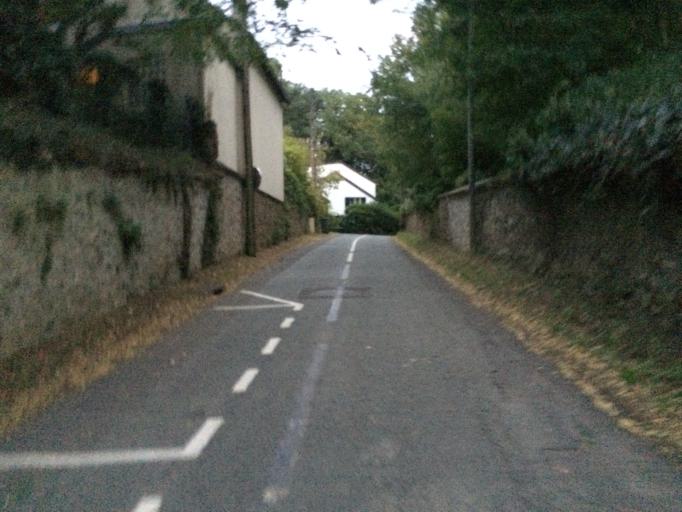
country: FR
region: Ile-de-France
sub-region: Departement de l'Essonne
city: Bievres
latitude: 48.7579
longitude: 2.2009
